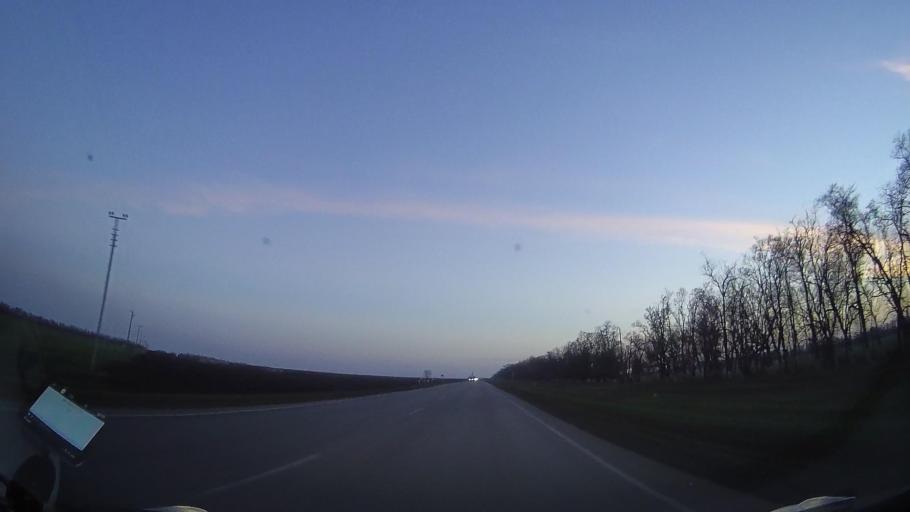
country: RU
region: Rostov
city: Zernograd
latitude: 46.8260
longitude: 40.2996
